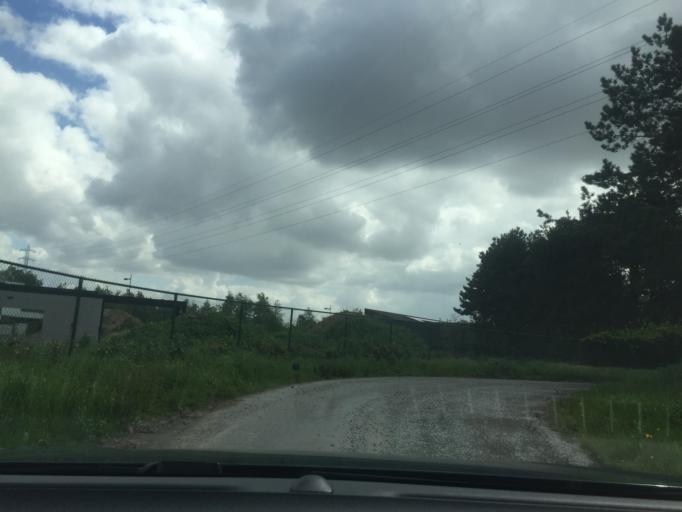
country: BE
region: Flanders
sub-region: Provincie West-Vlaanderen
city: Roeselare
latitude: 50.9299
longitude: 3.1472
